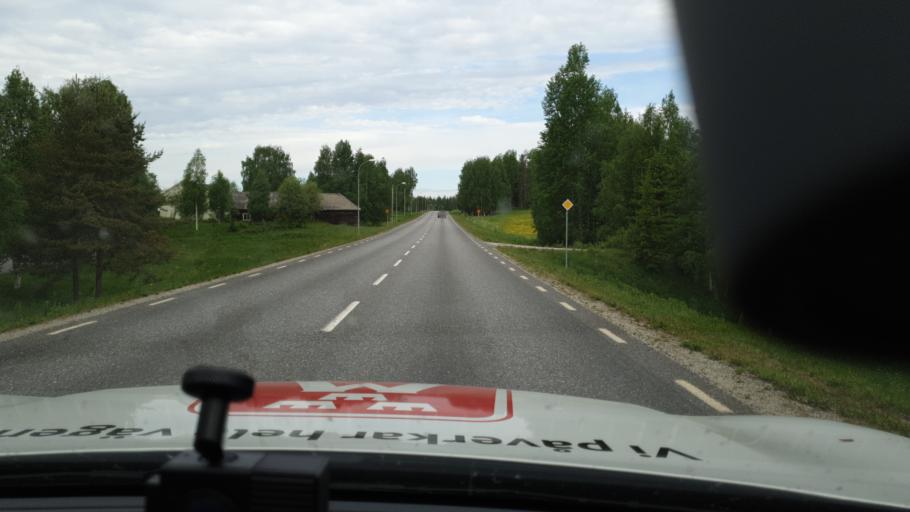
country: SE
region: Vaesterbotten
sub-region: Mala Kommun
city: Mala
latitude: 64.9882
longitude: 18.5054
